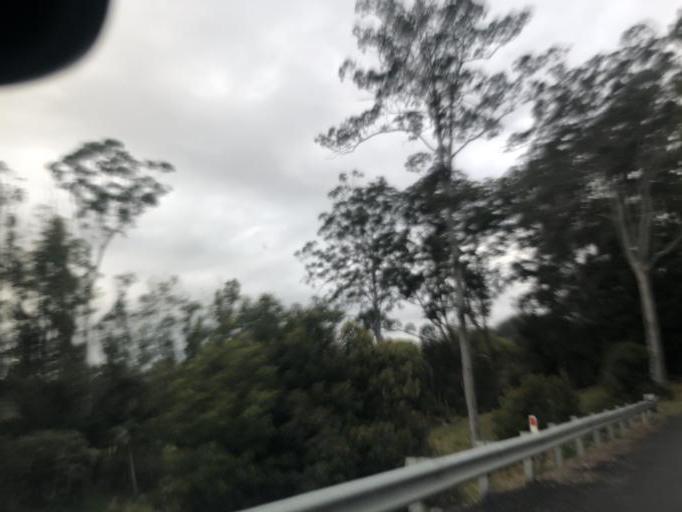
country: AU
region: New South Wales
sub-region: Coffs Harbour
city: Boambee
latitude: -30.2625
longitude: 153.0152
